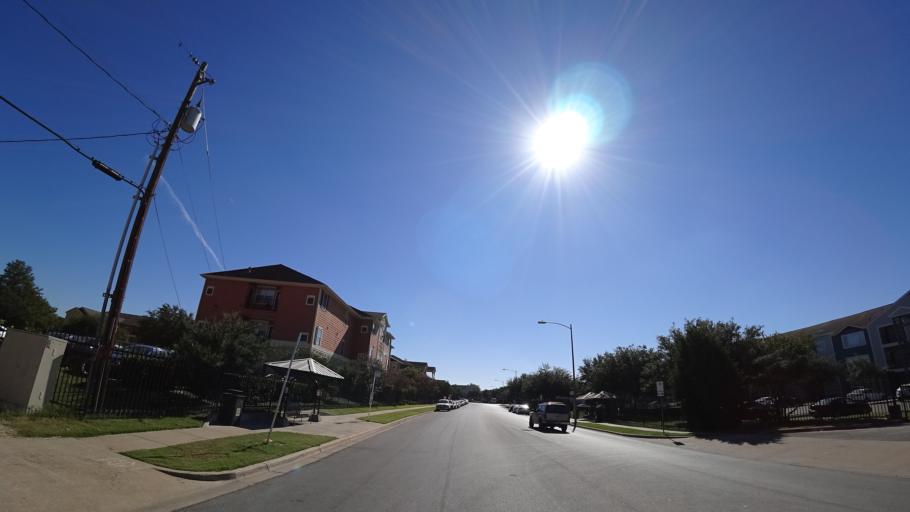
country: US
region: Texas
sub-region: Travis County
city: Austin
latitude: 30.2384
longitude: -97.7185
